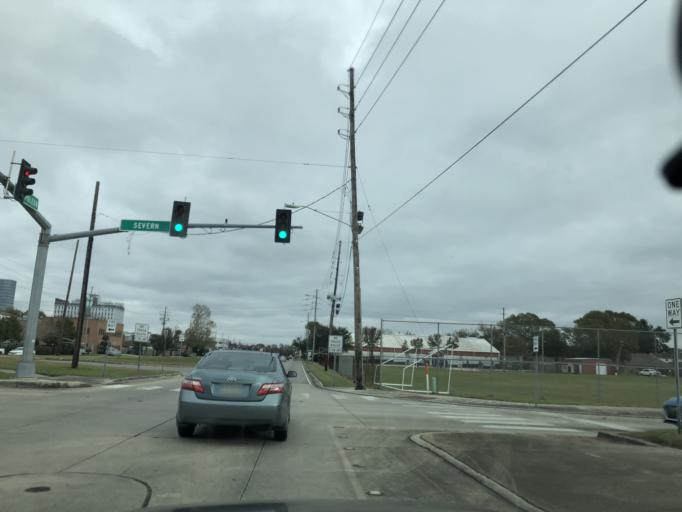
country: US
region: Louisiana
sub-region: Jefferson Parish
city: Metairie
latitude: 29.9923
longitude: -90.1600
